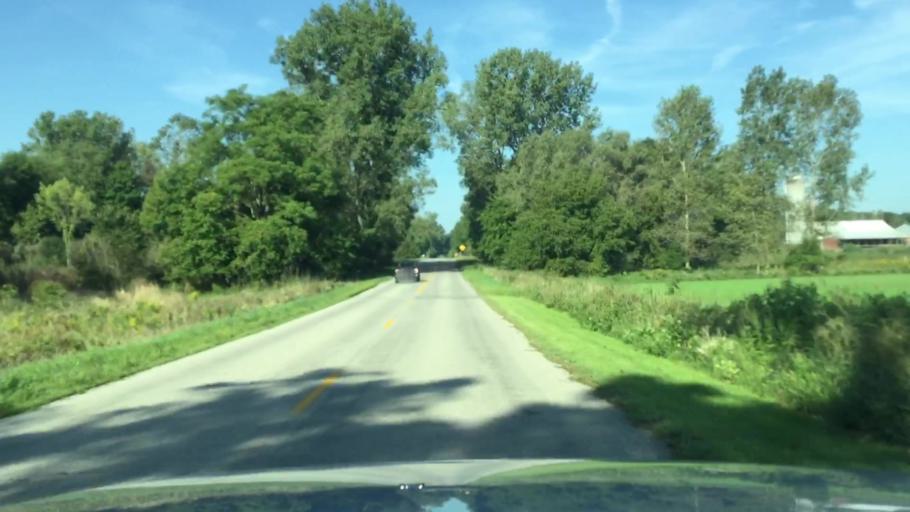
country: US
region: Michigan
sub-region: Lenawee County
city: Manitou Beach-Devils Lake
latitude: 41.9425
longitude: -84.3623
